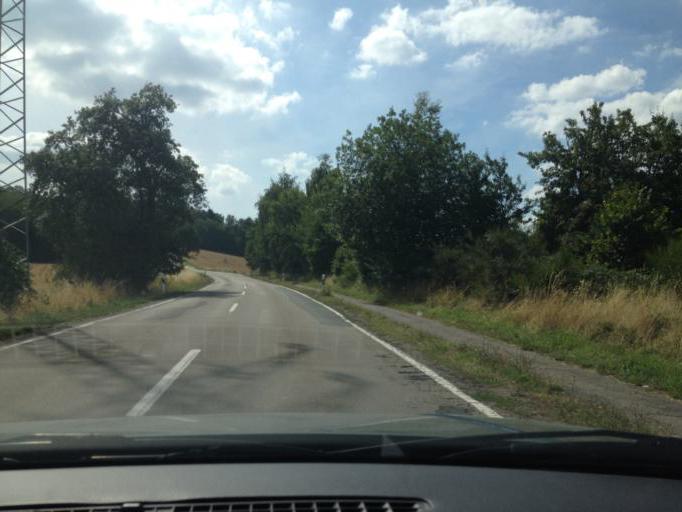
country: DE
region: Saarland
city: Ottweiler
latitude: 49.3992
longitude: 7.1442
